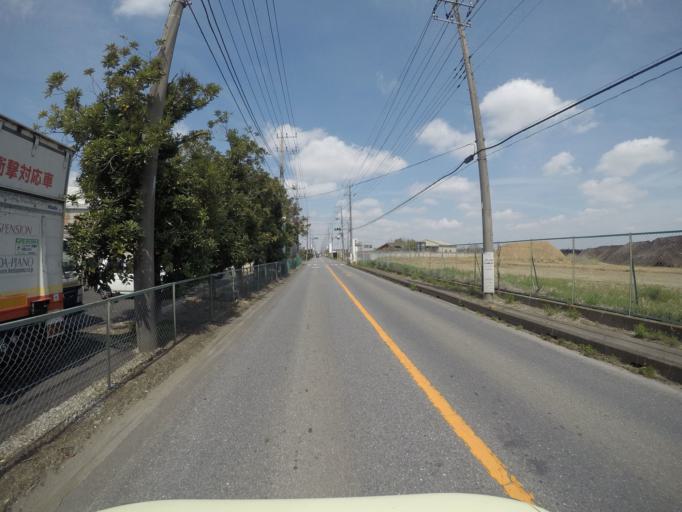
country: JP
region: Ibaraki
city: Tsukuba
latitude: 36.2326
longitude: 140.0564
